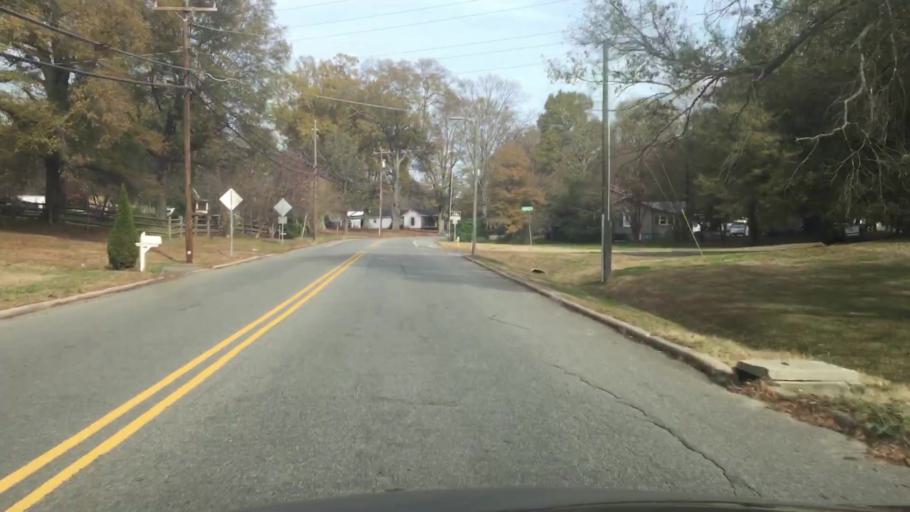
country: US
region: North Carolina
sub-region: Iredell County
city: Mooresville
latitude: 35.5805
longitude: -80.8294
